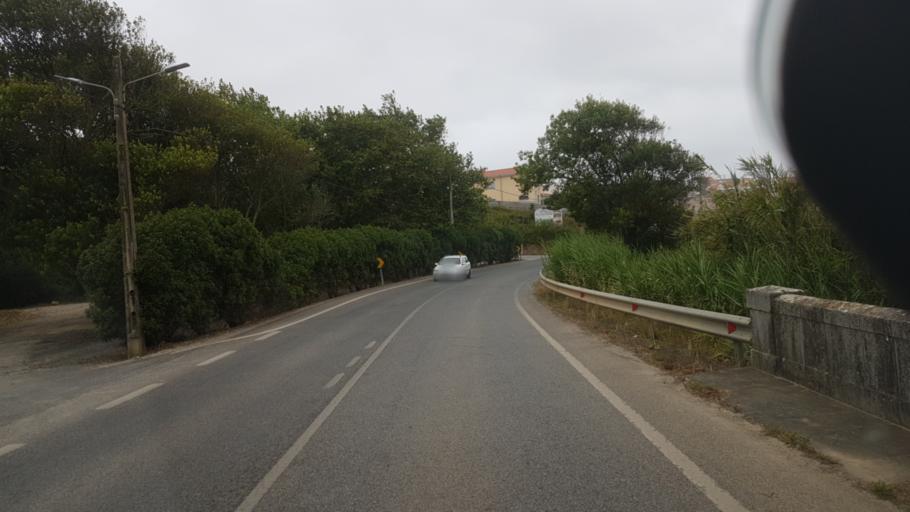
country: PT
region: Leiria
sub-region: Peniche
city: Atouguia da Baleia
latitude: 39.3374
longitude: -9.3220
